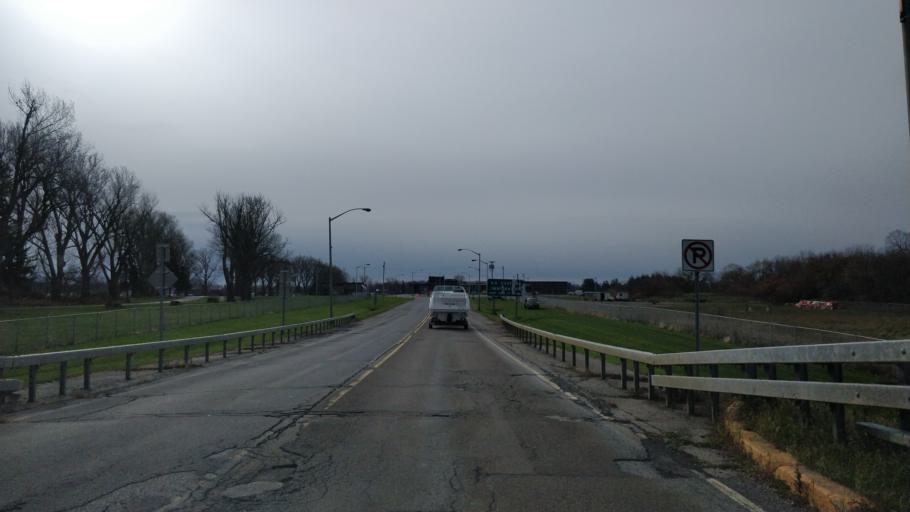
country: US
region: New York
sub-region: St. Lawrence County
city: Ogdensburg
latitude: 44.7259
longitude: -75.4551
